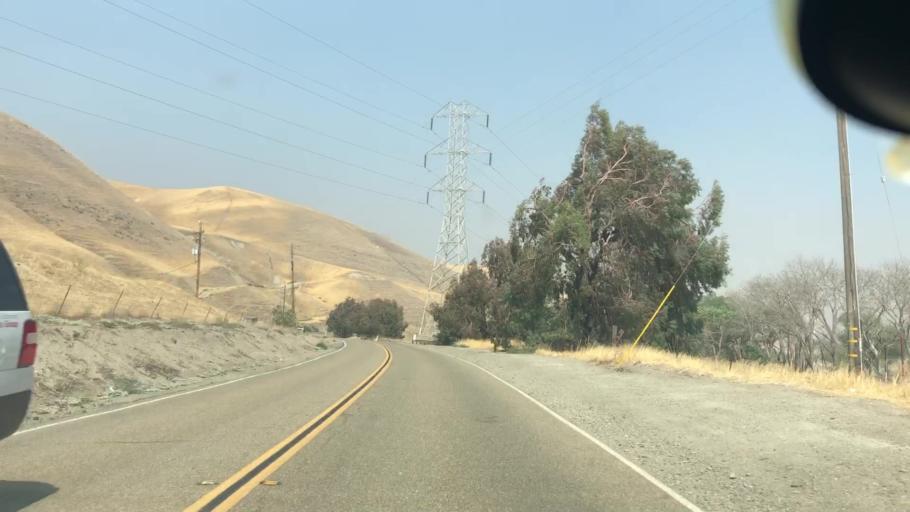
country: US
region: California
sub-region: San Joaquin County
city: Mountain House
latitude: 37.6377
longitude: -121.5737
